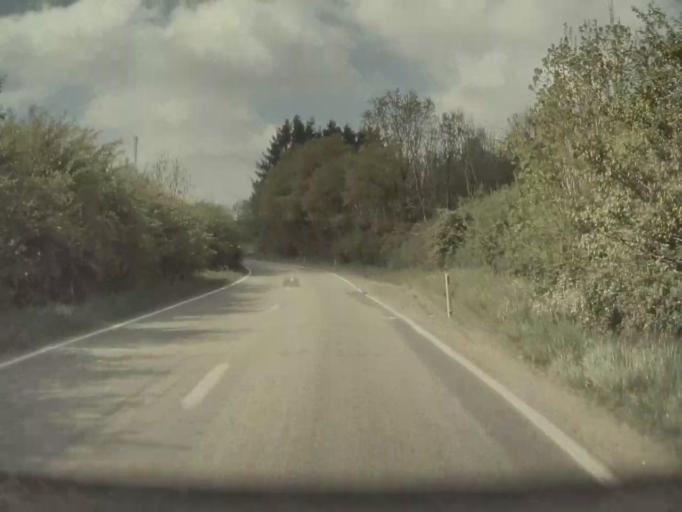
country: BE
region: Wallonia
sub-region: Province du Luxembourg
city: Tellin
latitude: 50.0737
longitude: 5.1988
